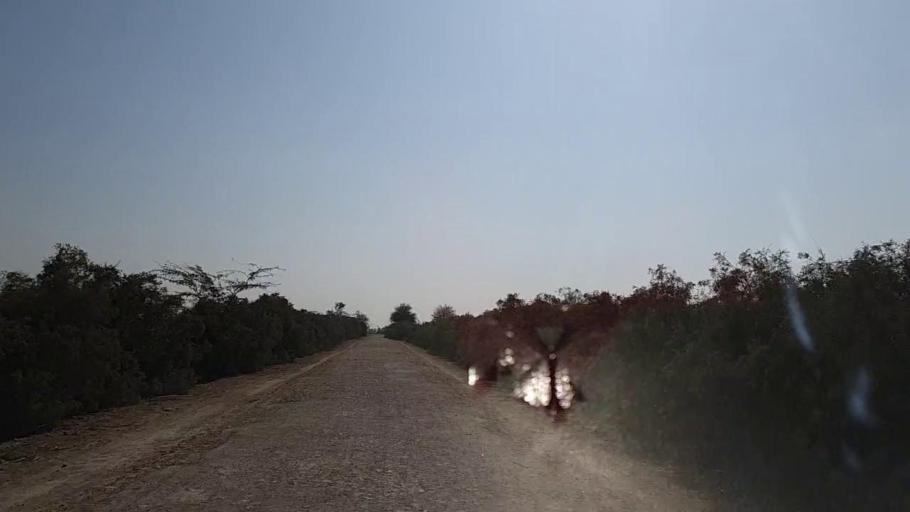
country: PK
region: Sindh
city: Sanghar
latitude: 26.0007
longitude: 69.0565
